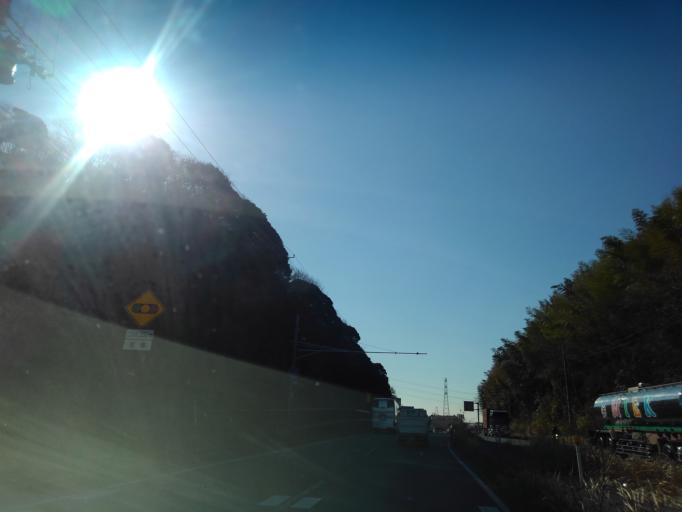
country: JP
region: Chiba
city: Kisarazu
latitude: 35.3457
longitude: 139.9211
